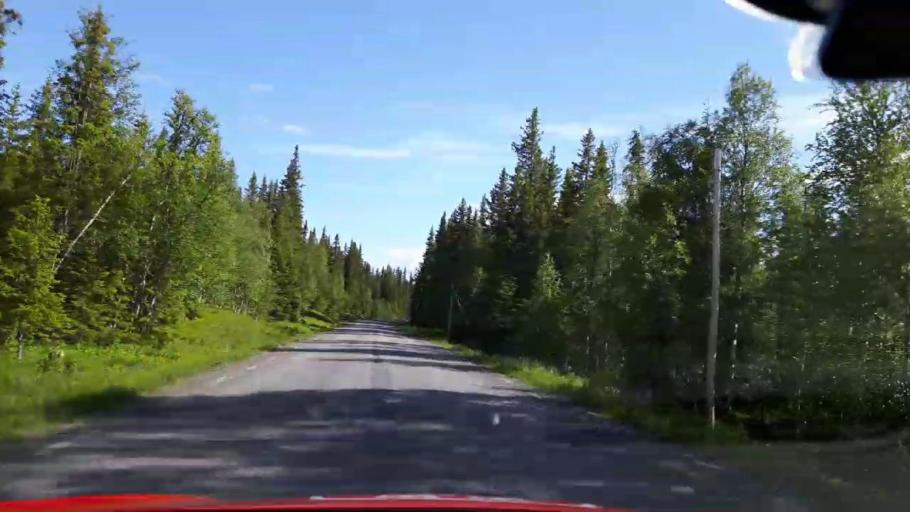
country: SE
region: Jaemtland
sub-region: Krokoms Kommun
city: Valla
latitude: 63.7389
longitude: 14.1182
